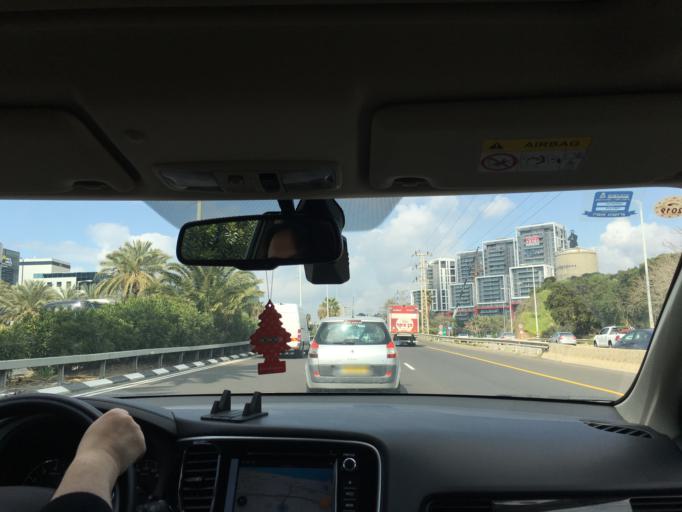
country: IL
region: Tel Aviv
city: Herzliyya
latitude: 32.1581
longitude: 34.8099
